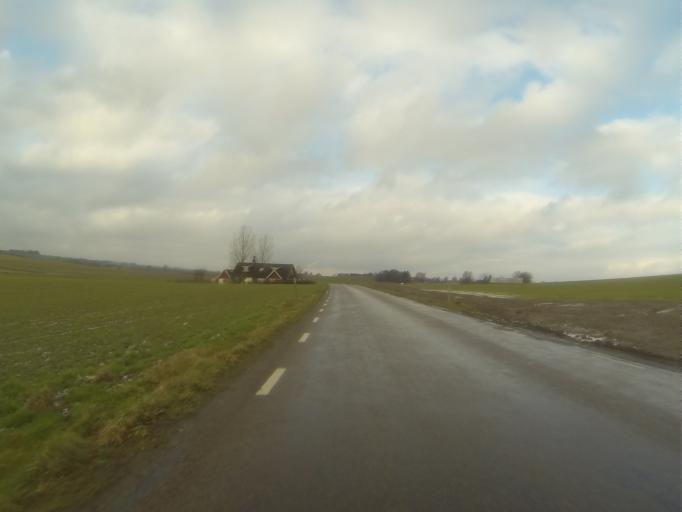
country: SE
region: Skane
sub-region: Svedala Kommun
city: Klagerup
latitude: 55.5745
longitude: 13.2992
